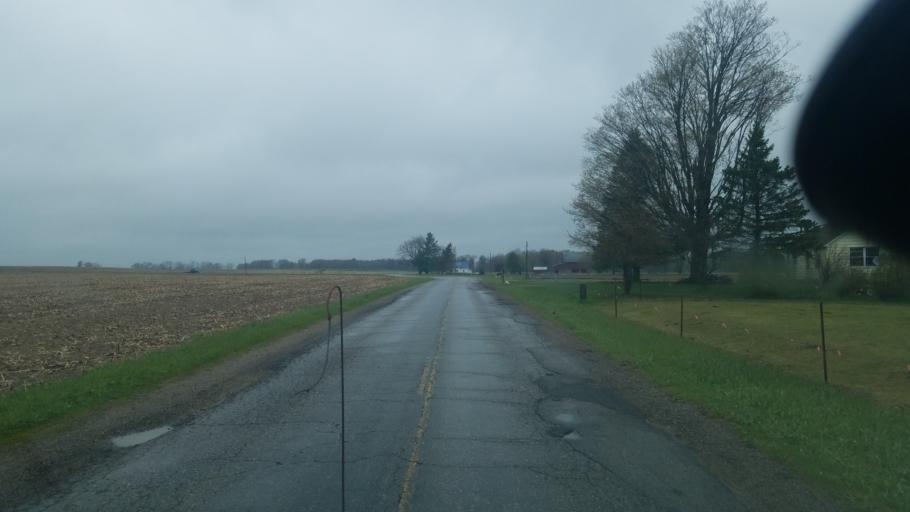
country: US
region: Michigan
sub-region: Mecosta County
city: Canadian Lakes
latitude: 43.5515
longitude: -85.3429
